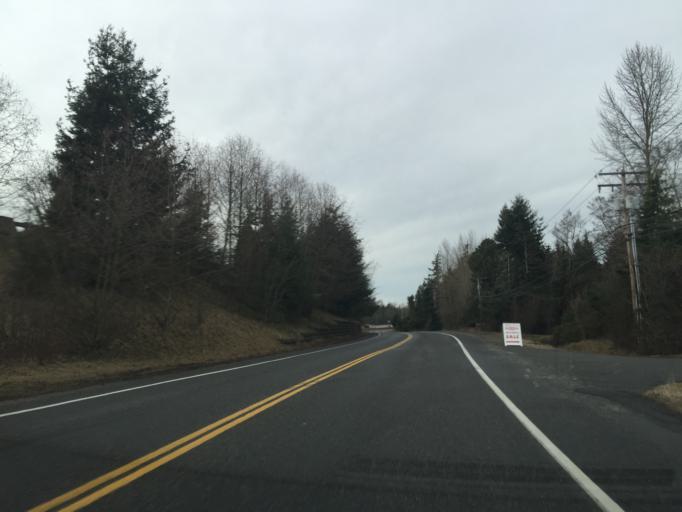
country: US
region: Washington
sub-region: Whatcom County
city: Marietta-Alderwood
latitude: 48.7899
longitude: -122.5186
